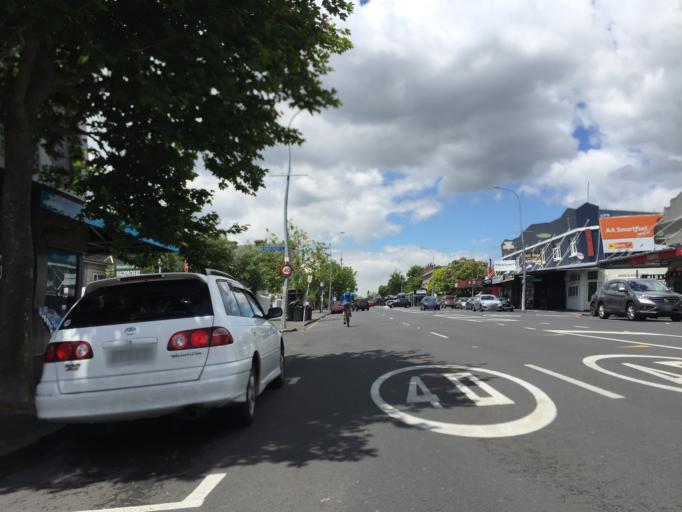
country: NZ
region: Auckland
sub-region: Auckland
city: Auckland
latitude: -36.8514
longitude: 174.7447
